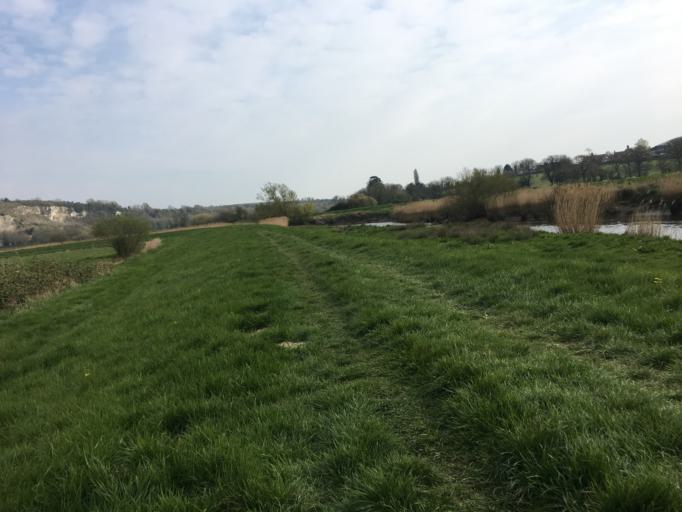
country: GB
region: England
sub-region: West Sussex
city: Arundel
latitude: 50.9001
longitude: -0.5515
